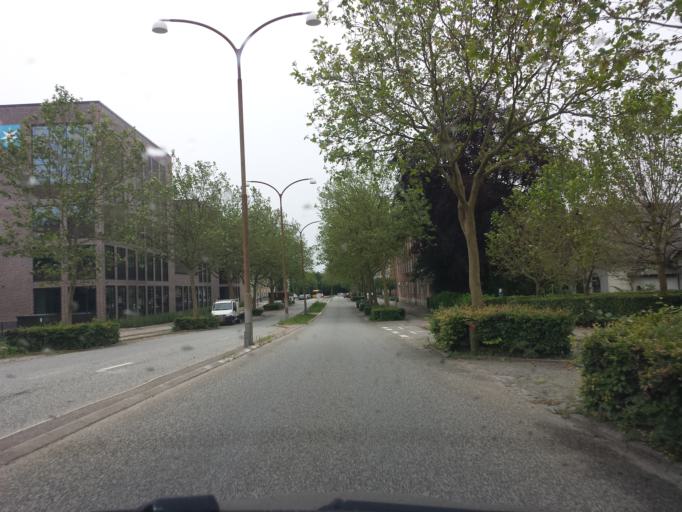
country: DK
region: Capital Region
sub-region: Lyngby-Tarbaek Kommune
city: Kongens Lyngby
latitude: 55.7655
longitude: 12.5095
